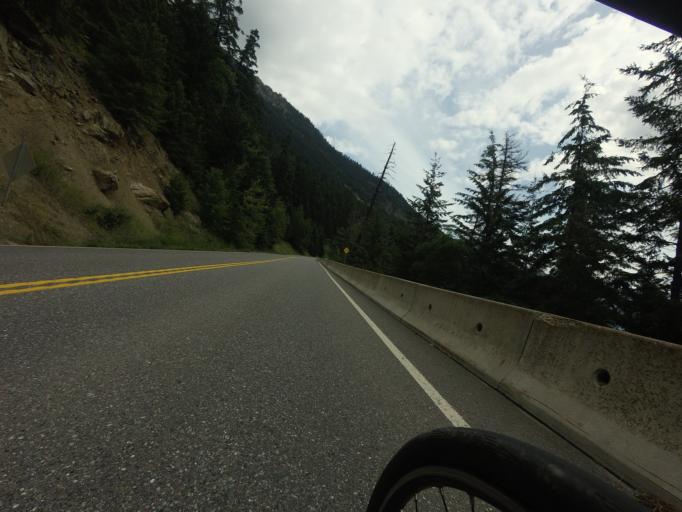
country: CA
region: British Columbia
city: Lillooet
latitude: 50.6466
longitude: -122.0224
